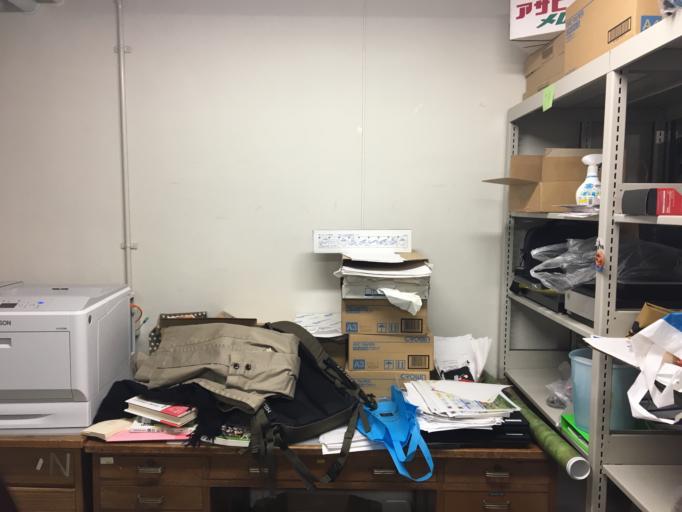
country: JP
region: Hokkaido
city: Ebetsu
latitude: 43.0741
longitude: 141.5117
